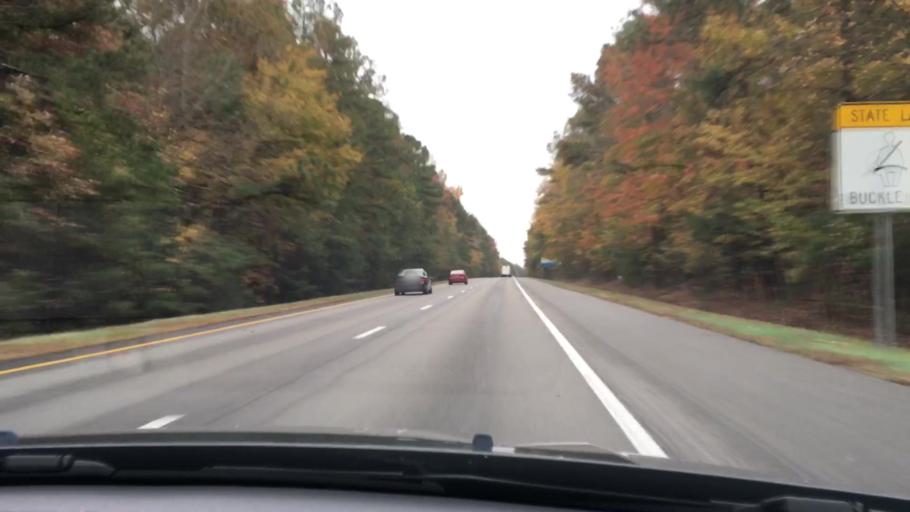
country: US
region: Virginia
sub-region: King William County
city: West Point
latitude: 37.4445
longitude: -76.8599
